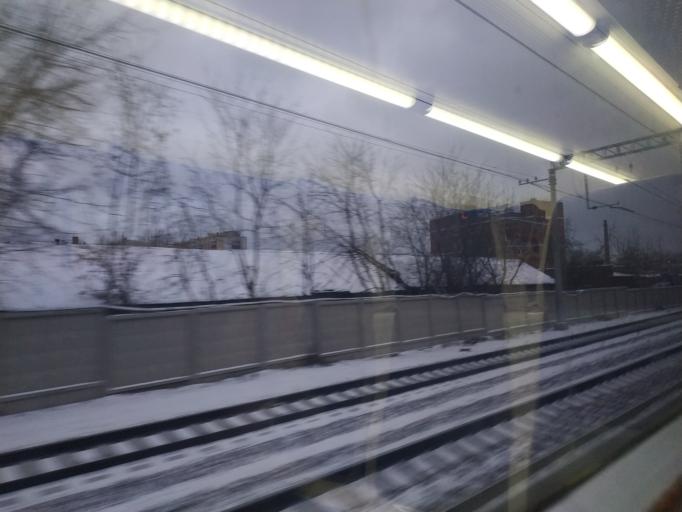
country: RU
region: Moscow
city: Lefortovo
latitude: 55.7354
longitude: 37.7078
